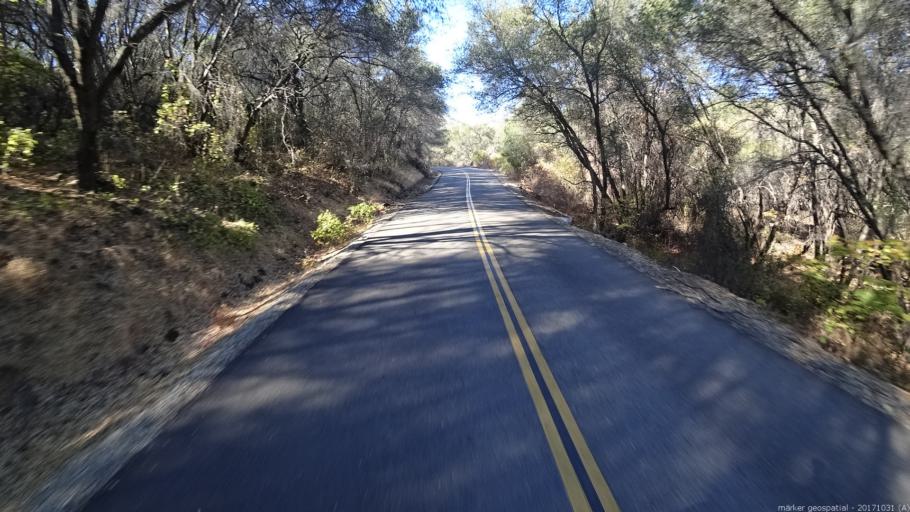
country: US
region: California
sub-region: Shasta County
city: Shingletown
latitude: 40.4412
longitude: -121.9864
